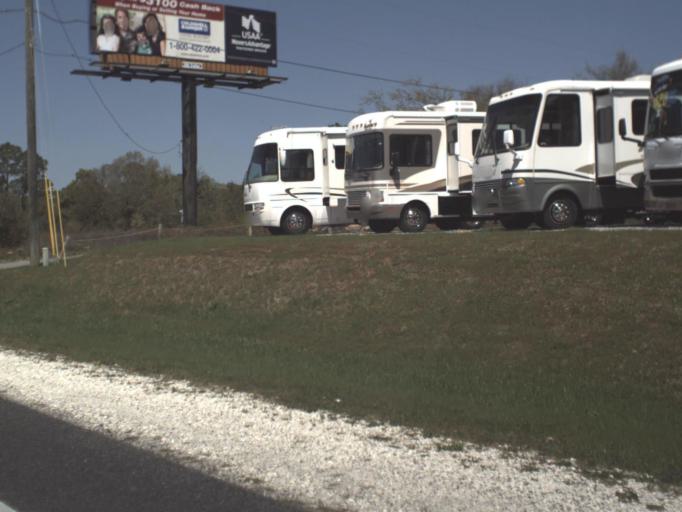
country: US
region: Florida
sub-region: Okaloosa County
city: Mary Esther
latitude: 30.4121
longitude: -86.7325
